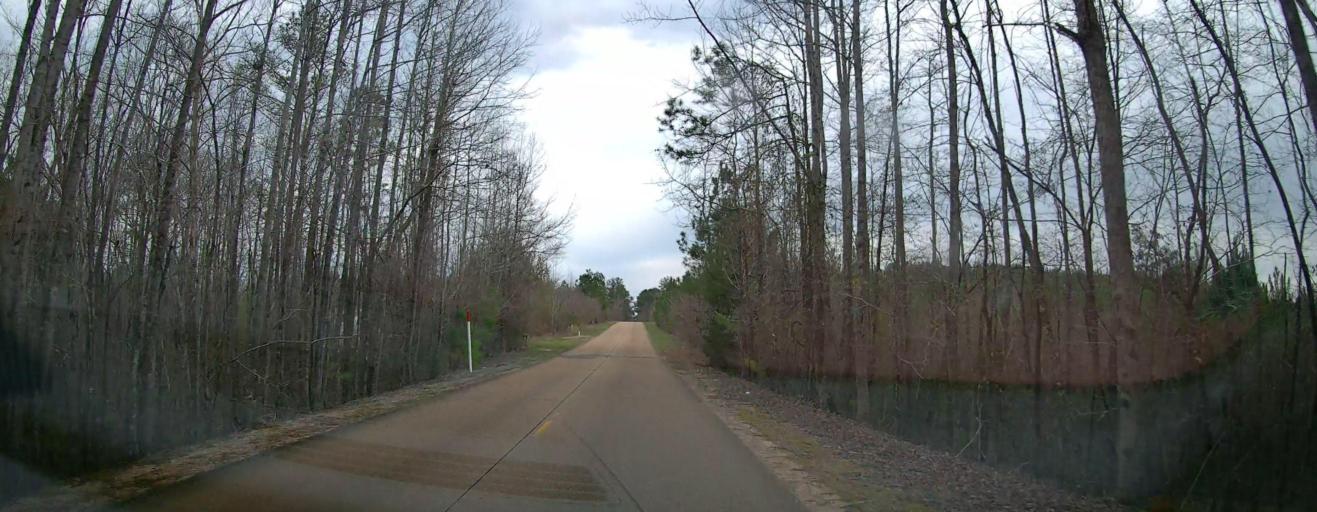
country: US
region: Mississippi
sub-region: Itawamba County
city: Fulton
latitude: 34.2119
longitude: -88.1992
